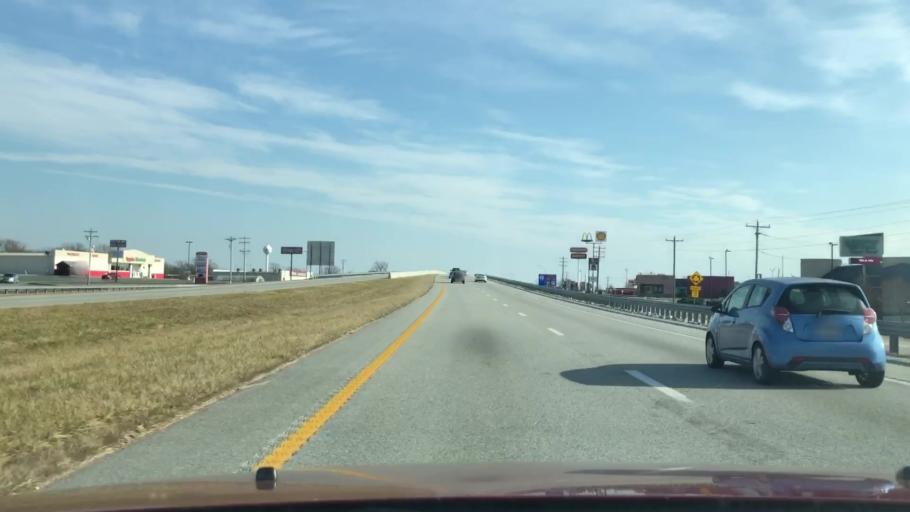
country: US
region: Missouri
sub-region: Webster County
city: Rogersville
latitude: 37.1096
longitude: -93.0608
